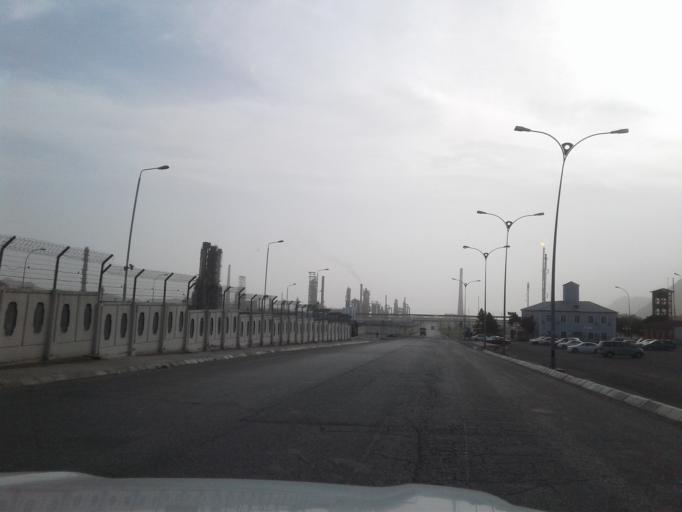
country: TM
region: Balkan
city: Turkmenbasy
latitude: 40.0339
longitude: 52.9554
